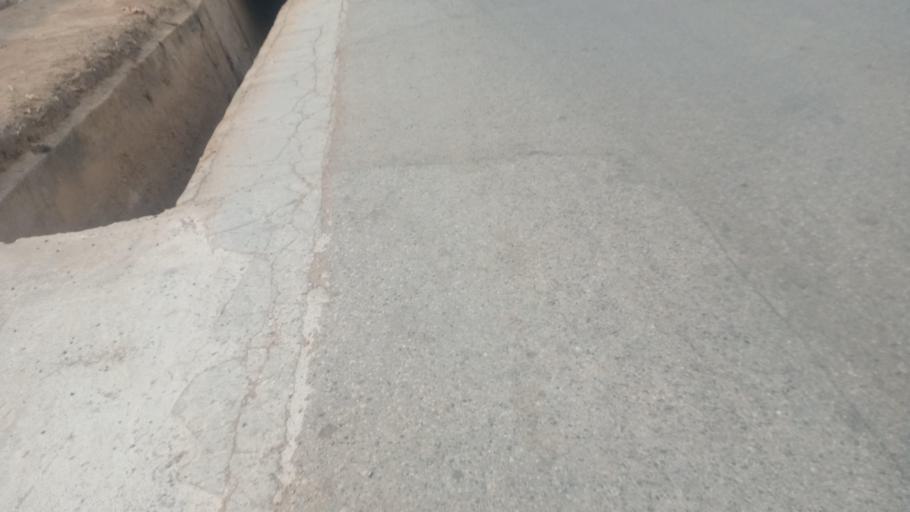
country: ZM
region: Lusaka
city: Lusaka
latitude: -15.4389
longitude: 28.3791
